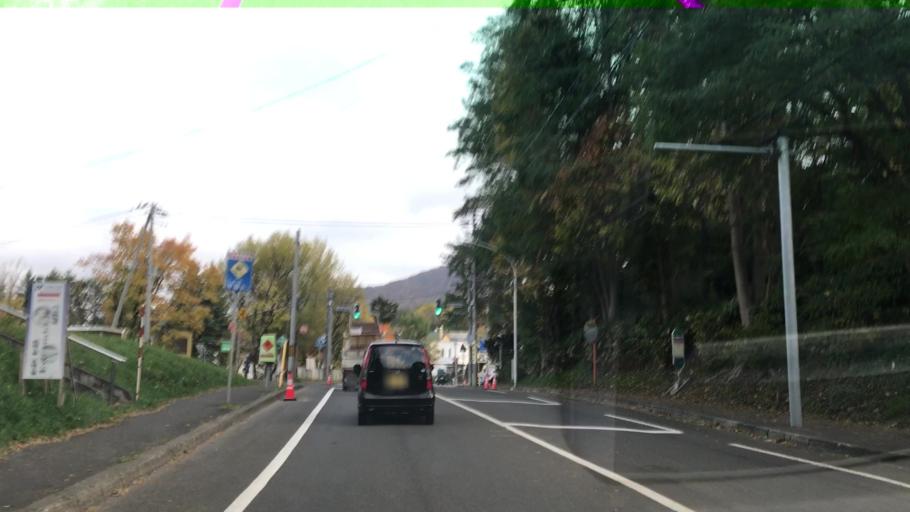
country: JP
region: Hokkaido
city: Sapporo
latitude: 43.0460
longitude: 141.3049
